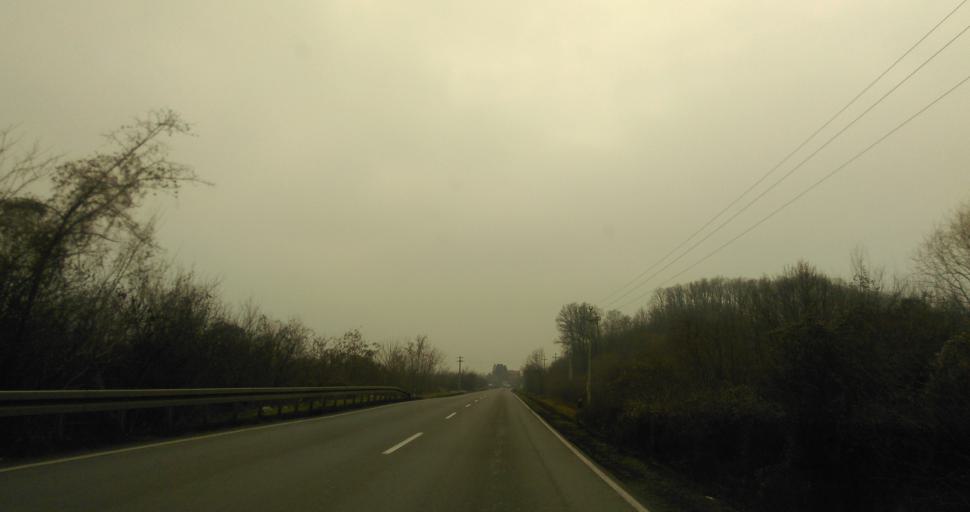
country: RS
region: Central Serbia
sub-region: Belgrade
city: Zvezdara
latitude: 44.7173
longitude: 20.5134
